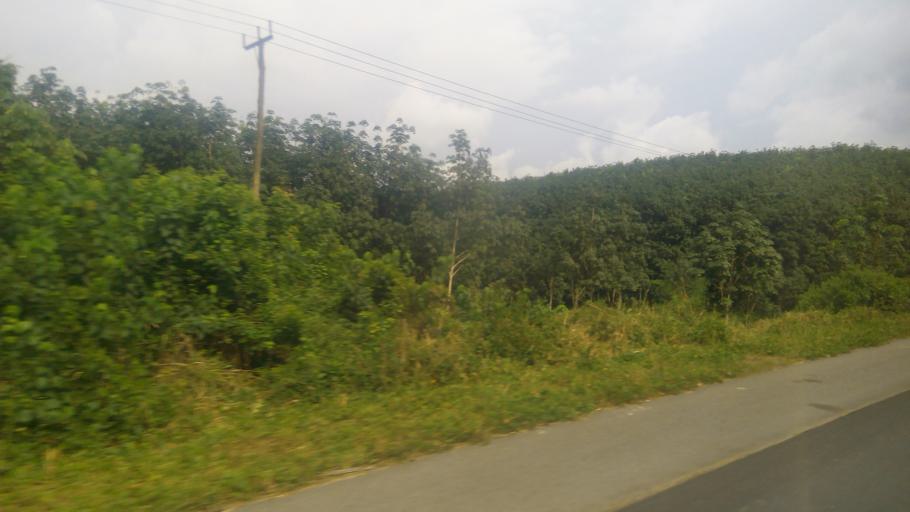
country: GH
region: Western
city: Axim
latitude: 4.9017
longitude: -2.1573
